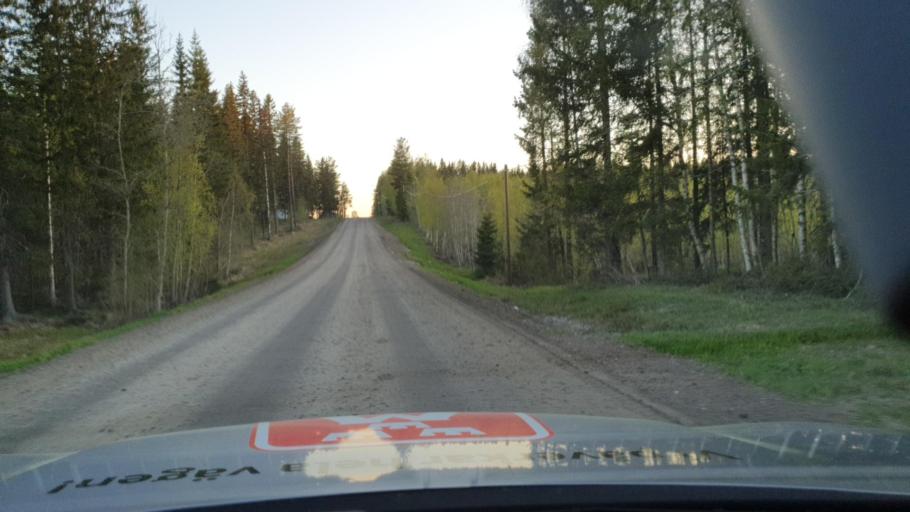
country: SE
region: Vaesternorrland
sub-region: OErnskoeldsviks Kommun
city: Ornskoldsvik
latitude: 63.5272
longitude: 18.5529
